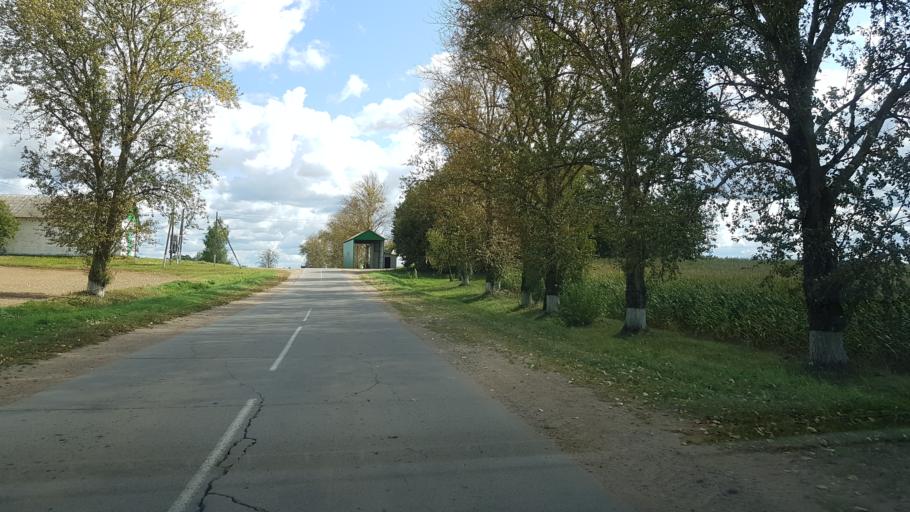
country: BY
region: Minsk
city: Dzyarzhynsk
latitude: 53.7360
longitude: 27.2154
